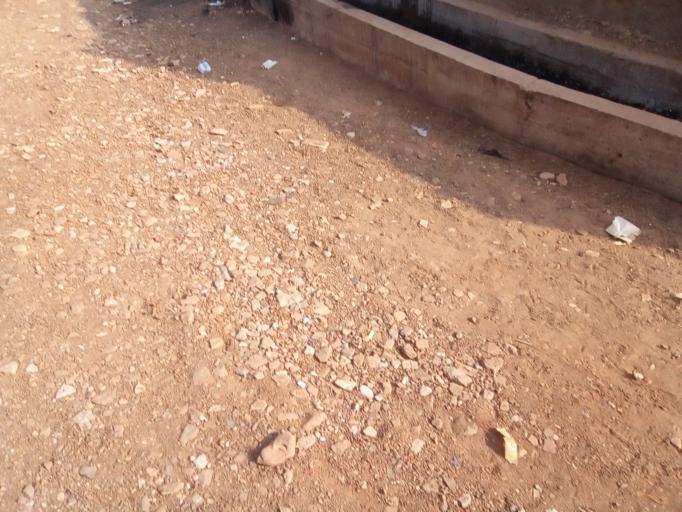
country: GH
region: Greater Accra
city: Accra
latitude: 5.5886
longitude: -0.2136
